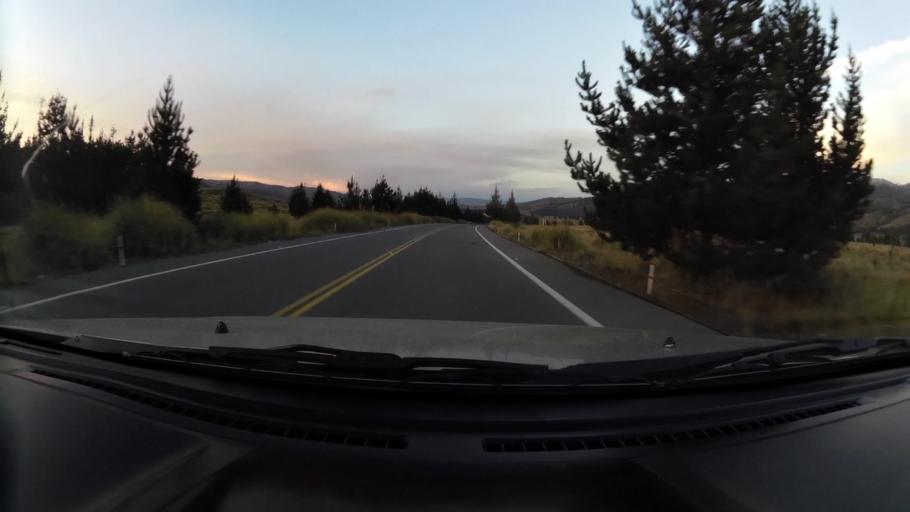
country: EC
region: Chimborazo
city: Alausi
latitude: -2.0277
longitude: -78.7346
